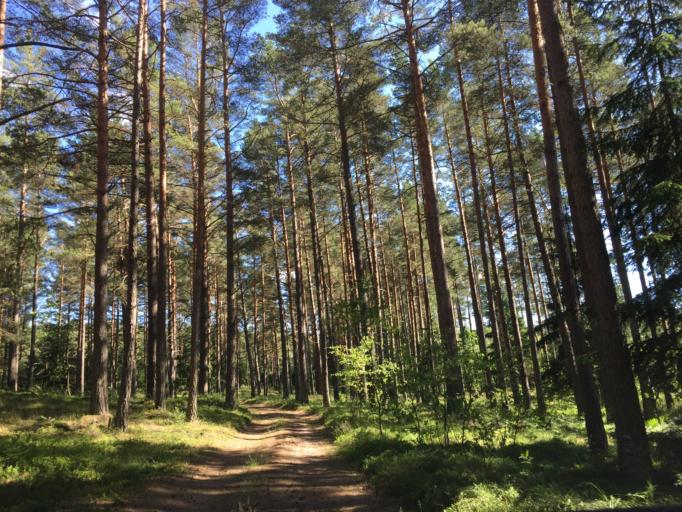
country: LV
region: Ventspils
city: Ventspils
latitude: 57.4664
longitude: 21.6523
